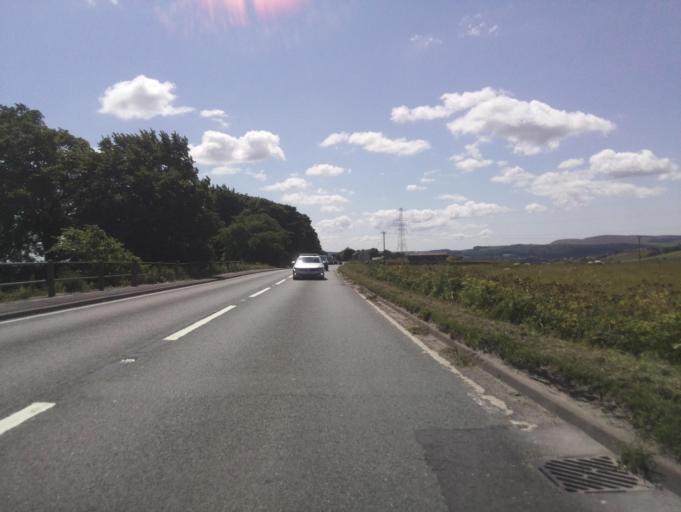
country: GB
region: England
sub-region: Derbyshire
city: Buxton
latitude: 53.2850
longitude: -1.8896
